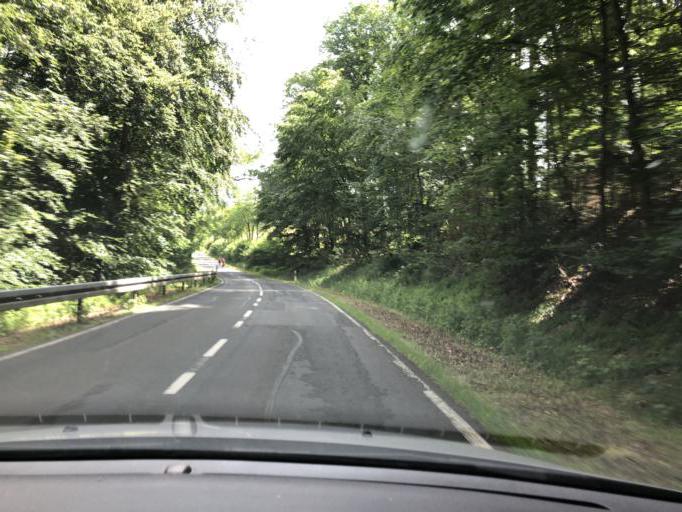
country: DE
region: Hesse
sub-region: Regierungsbezirk Kassel
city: Malsfeld
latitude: 51.0709
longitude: 9.5534
